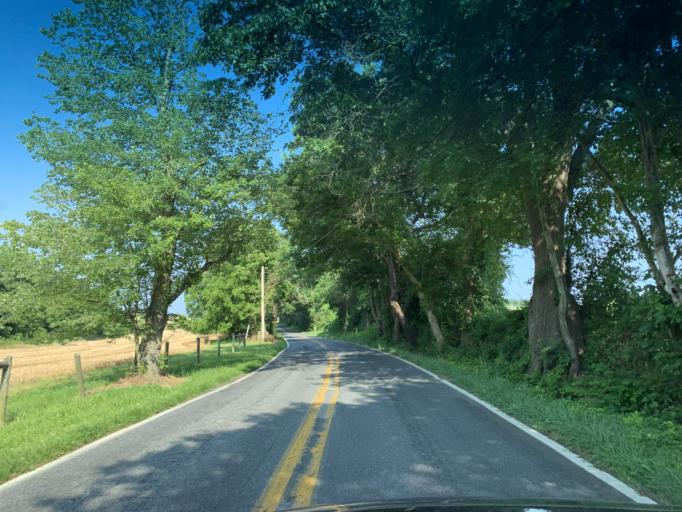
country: US
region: Maryland
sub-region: Frederick County
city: Urbana
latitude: 39.2481
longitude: -77.3614
